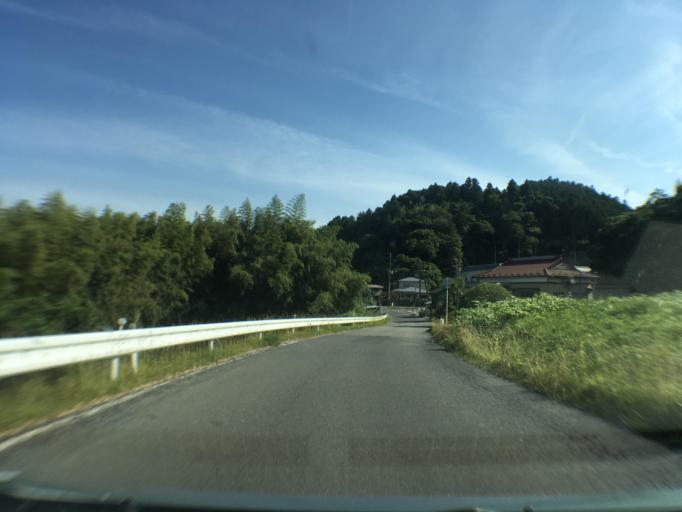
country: JP
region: Miyagi
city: Wakuya
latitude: 38.6493
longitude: 141.2820
